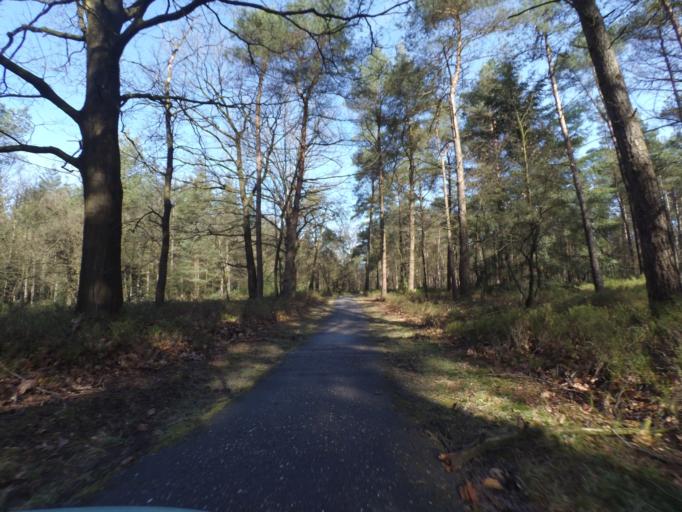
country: NL
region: Gelderland
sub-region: Gemeente Apeldoorn
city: Uddel
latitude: 52.2060
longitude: 5.8100
